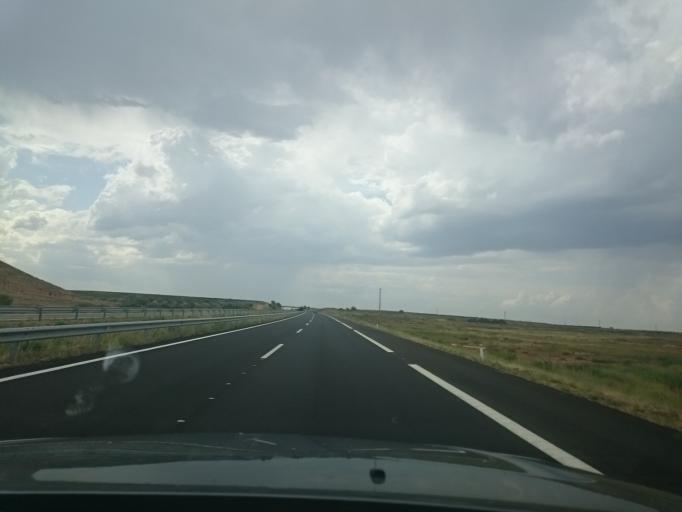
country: ES
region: La Rioja
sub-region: Provincia de La Rioja
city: Rincon de Soto
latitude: 42.2022
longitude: -1.8576
